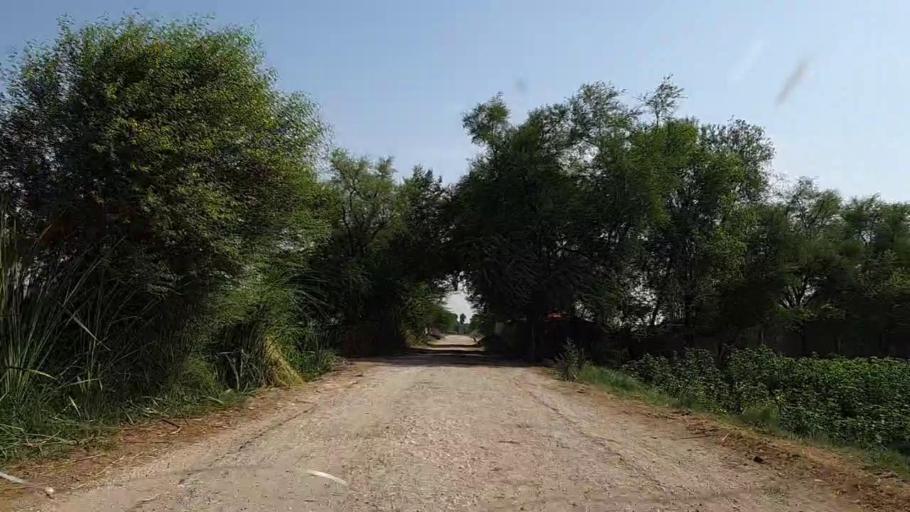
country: PK
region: Sindh
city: Khanpur
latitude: 27.7427
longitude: 69.3420
